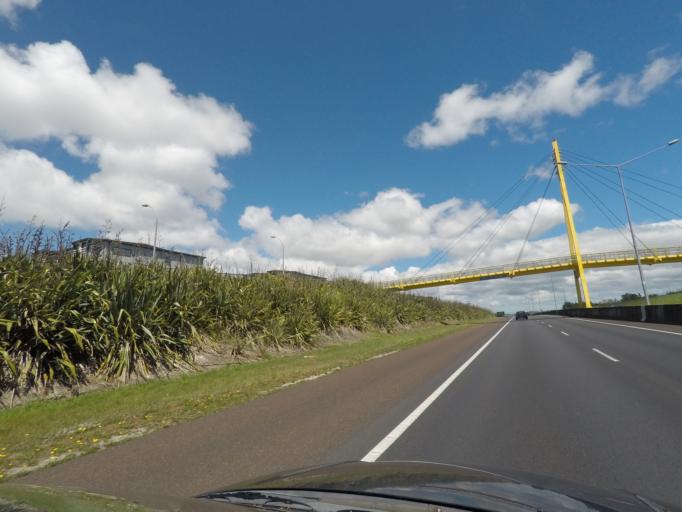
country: NZ
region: Auckland
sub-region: Auckland
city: Rosebank
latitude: -36.7951
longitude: 174.6479
